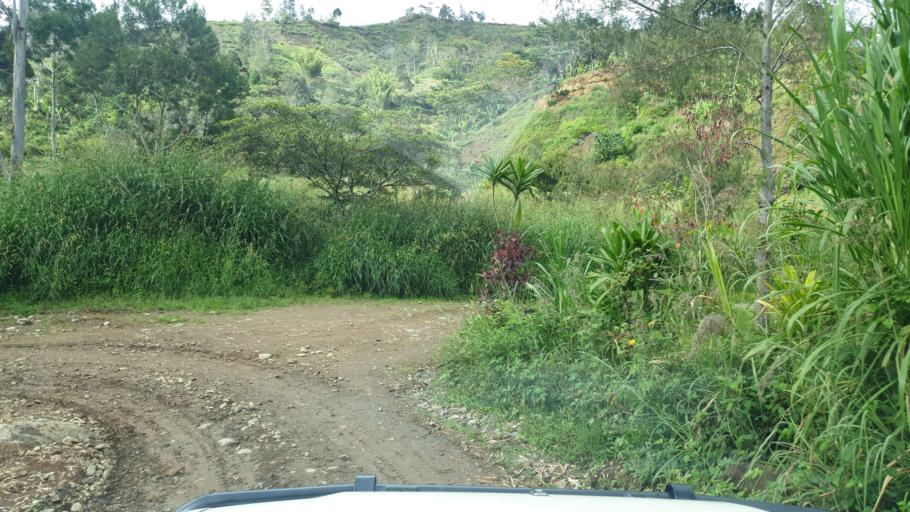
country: PG
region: Eastern Highlands
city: Goroka
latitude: -5.9356
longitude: 145.2669
